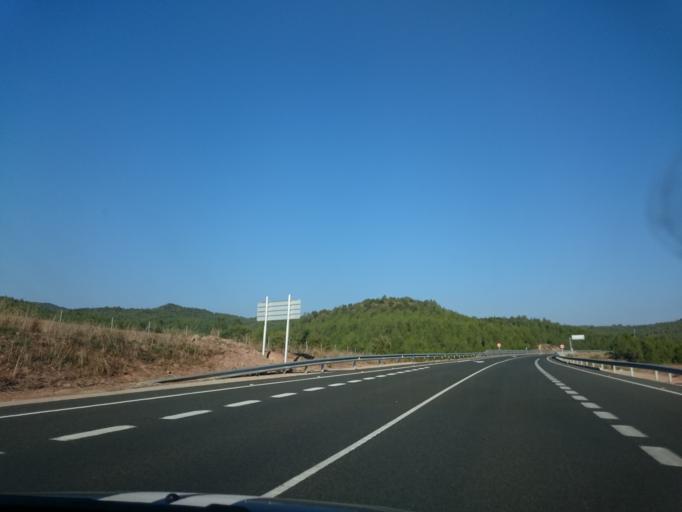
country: ES
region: Catalonia
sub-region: Provincia de Barcelona
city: Sant Salvador de Guardiola
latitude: 41.6983
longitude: 1.7798
